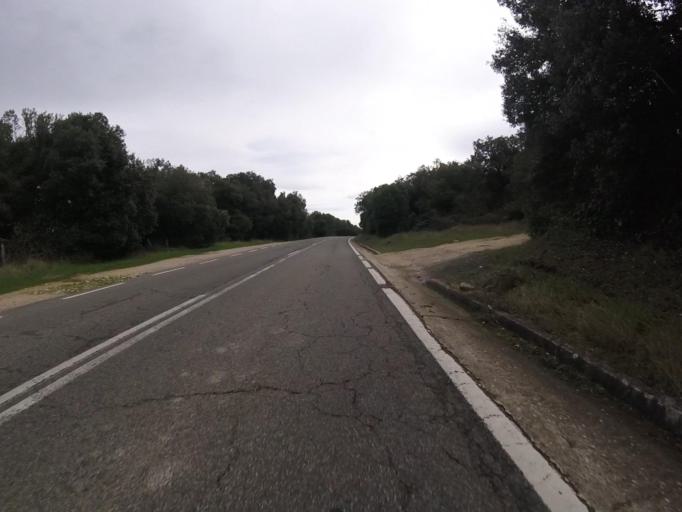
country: ES
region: Navarre
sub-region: Provincia de Navarra
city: Lezaun
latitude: 42.7512
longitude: -2.0155
